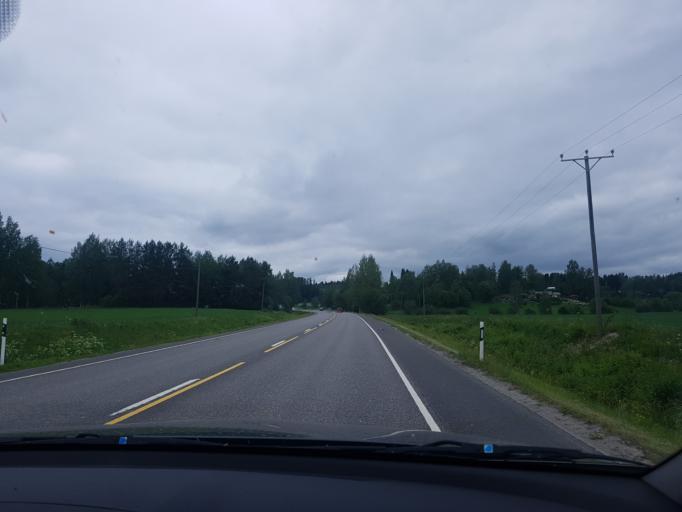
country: FI
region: Pirkanmaa
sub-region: Tampere
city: Paelkaene
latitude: 61.2817
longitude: 24.3362
